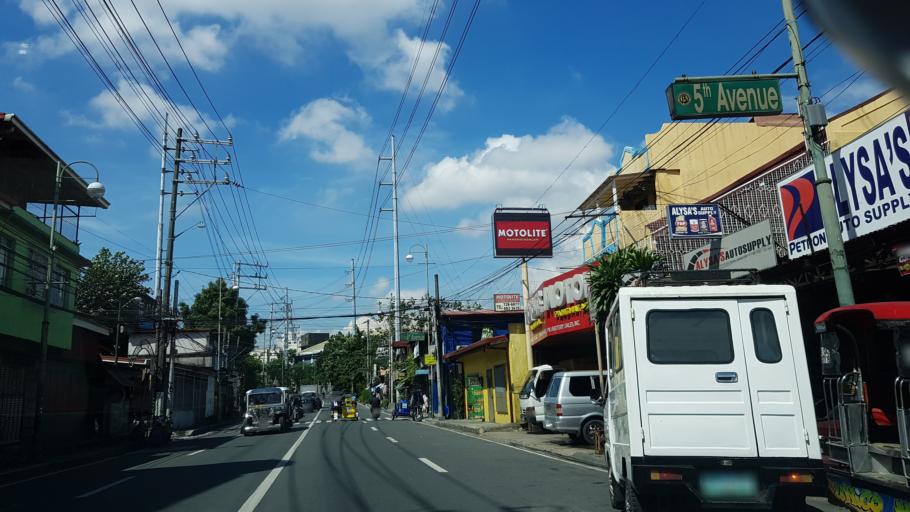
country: PH
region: Calabarzon
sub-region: Province of Rizal
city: Pateros
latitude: 14.5566
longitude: 121.0654
